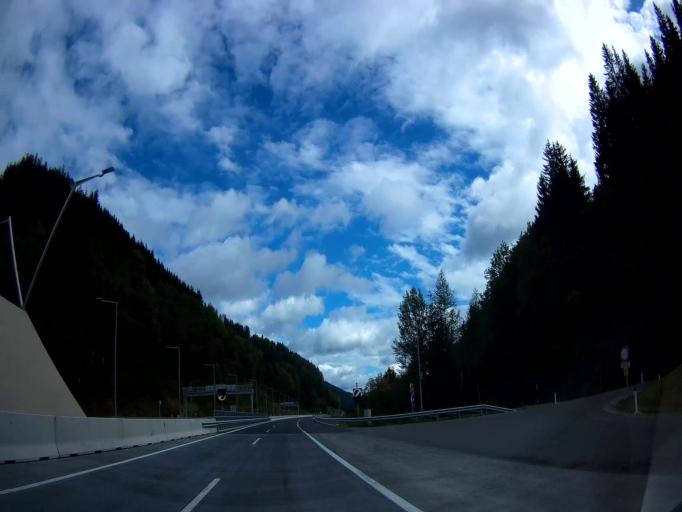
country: AT
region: Styria
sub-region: Politischer Bezirk Leoben
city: Leoben
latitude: 47.2942
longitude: 15.0783
